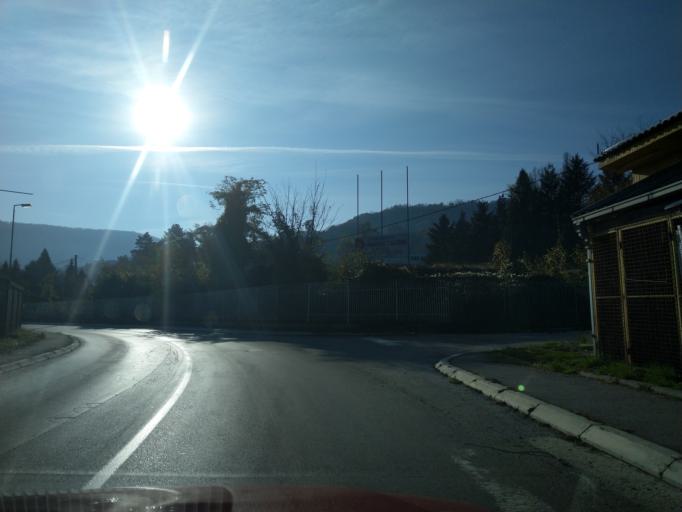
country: RS
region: Central Serbia
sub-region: Zlatiborski Okrug
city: Uzice
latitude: 43.8442
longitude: 19.8873
